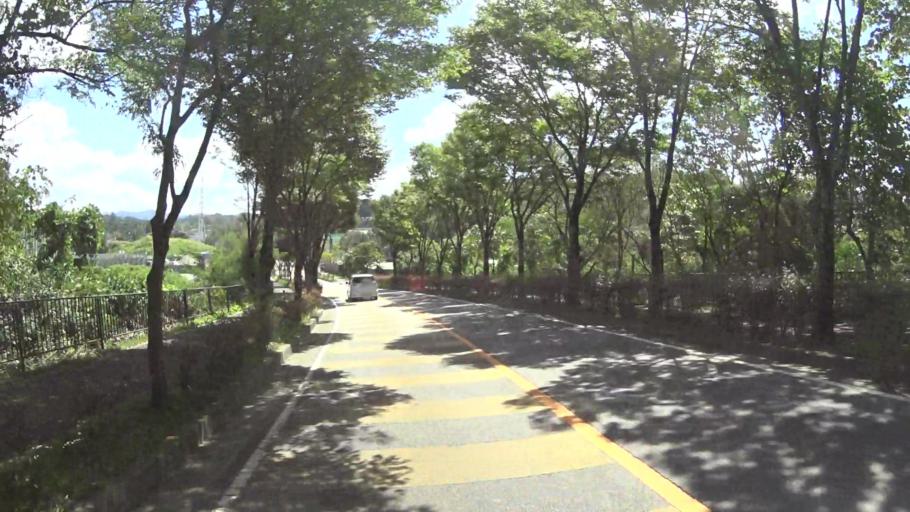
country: JP
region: Kyoto
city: Uji
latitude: 34.8638
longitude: 135.7971
